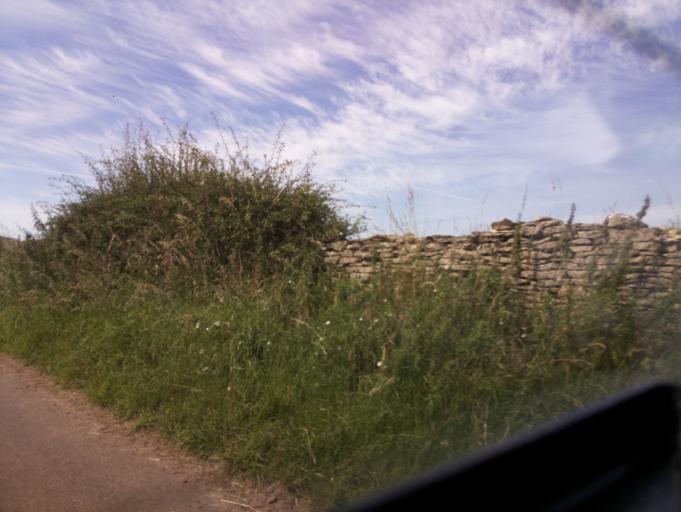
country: GB
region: England
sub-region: Wiltshire
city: Nettleton
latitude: 51.5252
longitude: -2.3090
